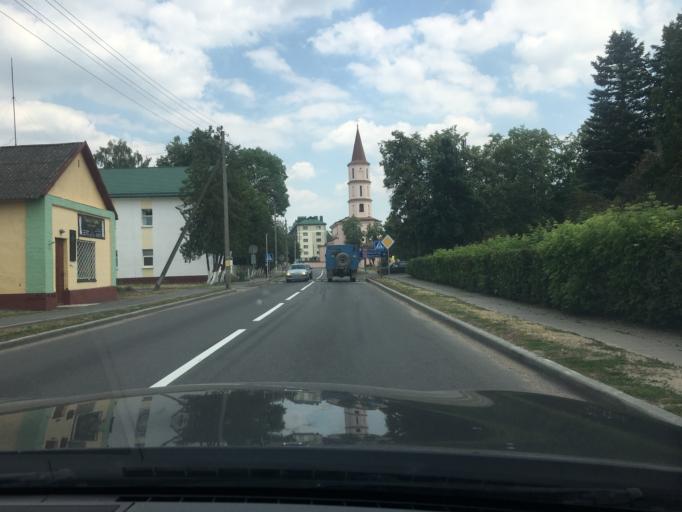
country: BY
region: Brest
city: Ruzhany
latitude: 52.8669
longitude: 24.8884
